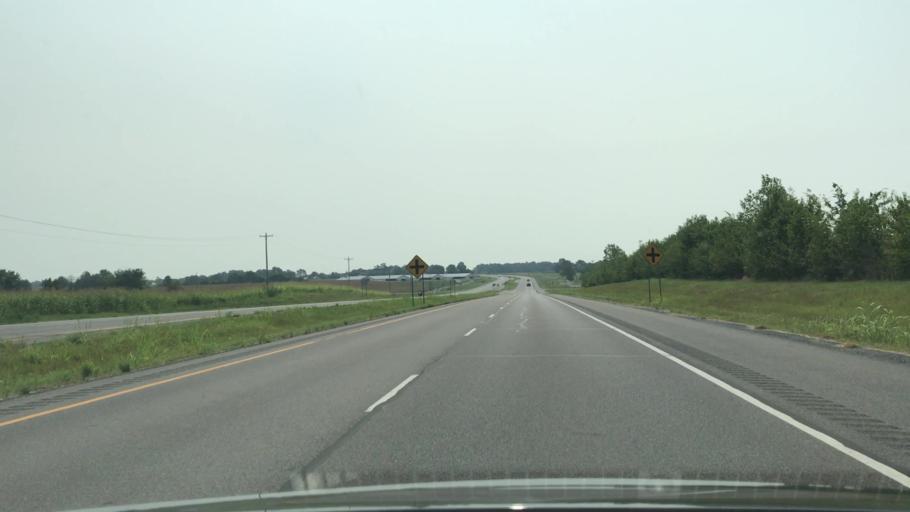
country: US
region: Kentucky
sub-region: Graves County
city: Mayfield
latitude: 36.6832
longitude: -88.5367
